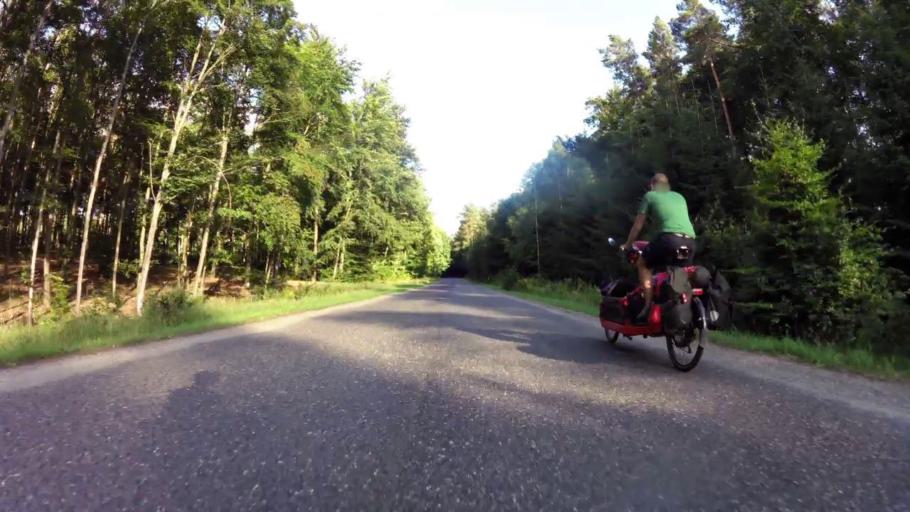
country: PL
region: West Pomeranian Voivodeship
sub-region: Powiat drawski
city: Drawsko Pomorskie
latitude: 53.4700
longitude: 15.8340
